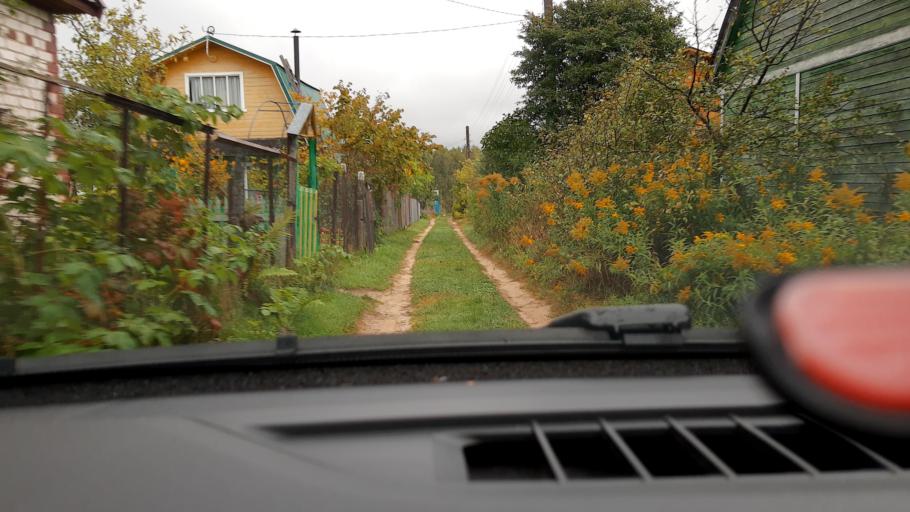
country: RU
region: Nizjnij Novgorod
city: Burevestnik
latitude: 56.1026
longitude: 43.9540
